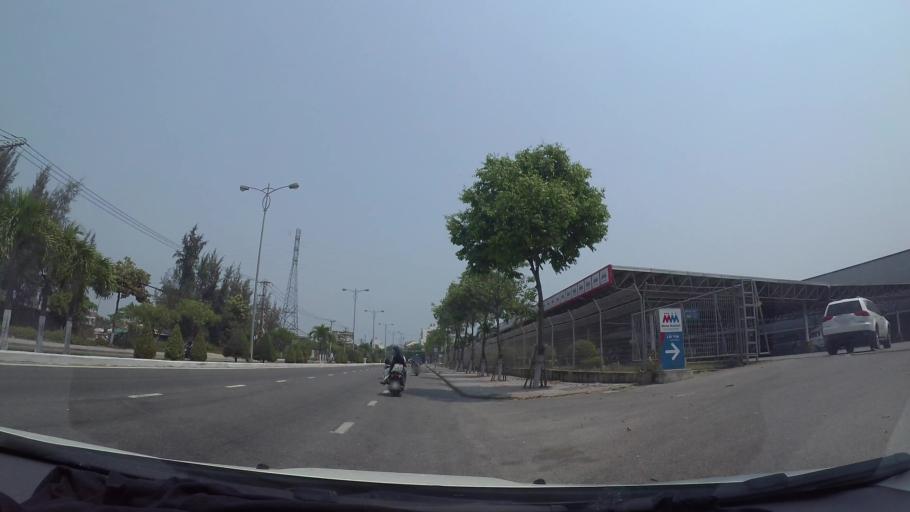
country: VN
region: Da Nang
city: Cam Le
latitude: 16.0253
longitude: 108.2194
